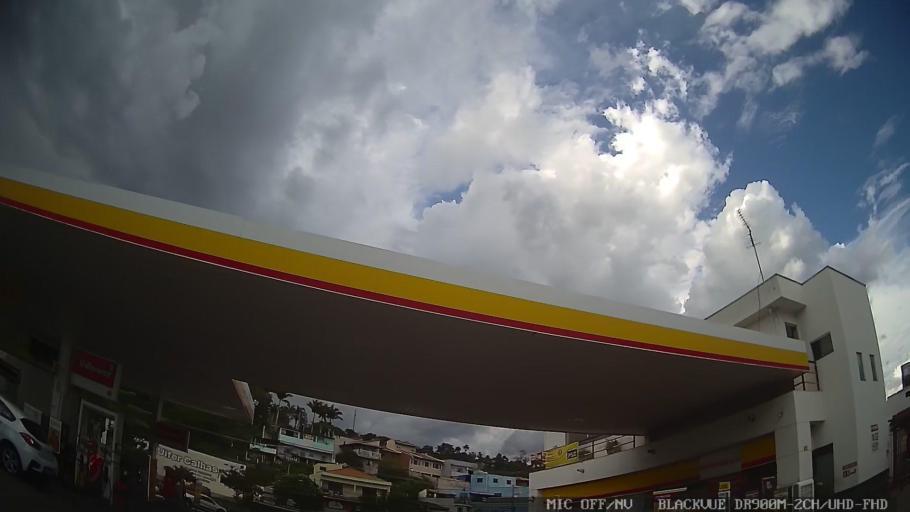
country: BR
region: Sao Paulo
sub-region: Pedreira
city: Pedreira
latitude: -22.7313
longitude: -46.8958
